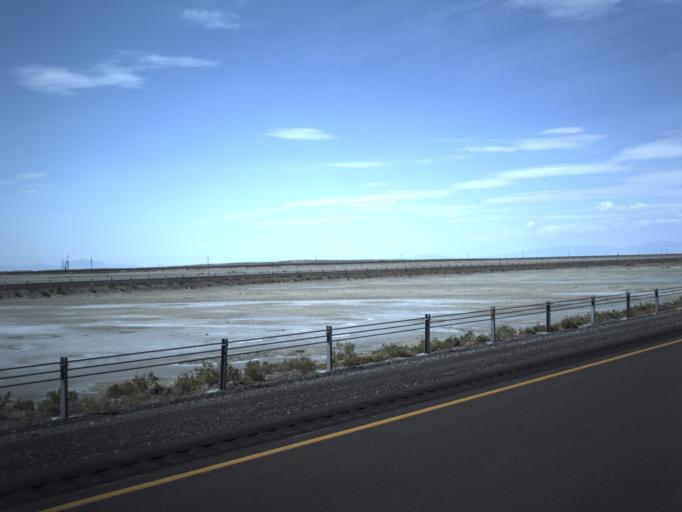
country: US
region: Utah
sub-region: Tooele County
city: Wendover
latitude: 40.7285
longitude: -113.3368
